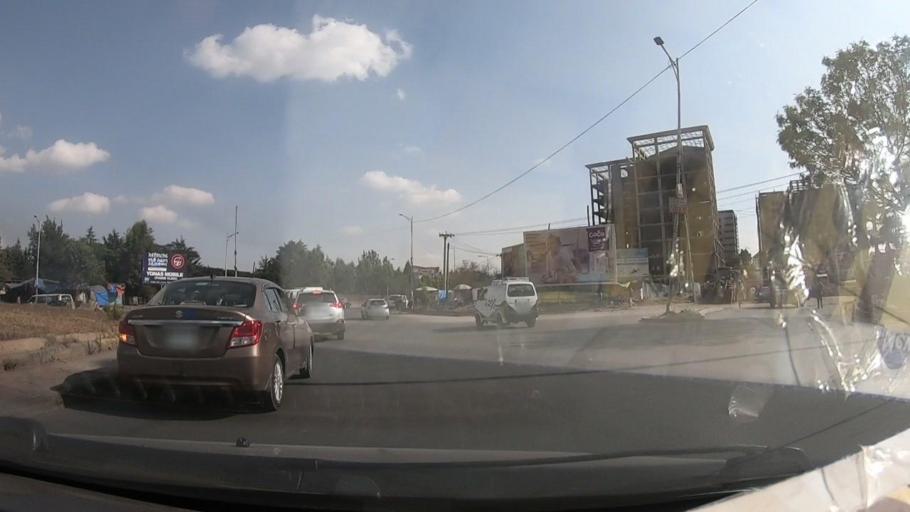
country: ET
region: Adis Abeba
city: Addis Ababa
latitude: 8.9645
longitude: 38.7321
